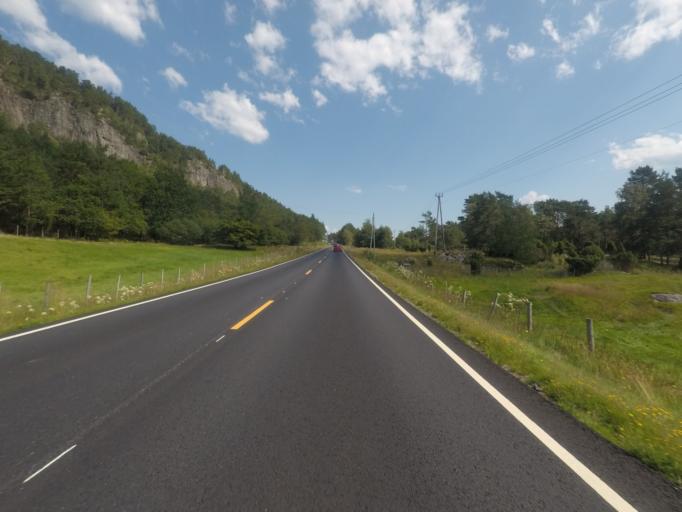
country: NO
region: Sogn og Fjordane
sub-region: Hyllestad
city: Hyllestad
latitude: 61.1166
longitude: 5.5593
